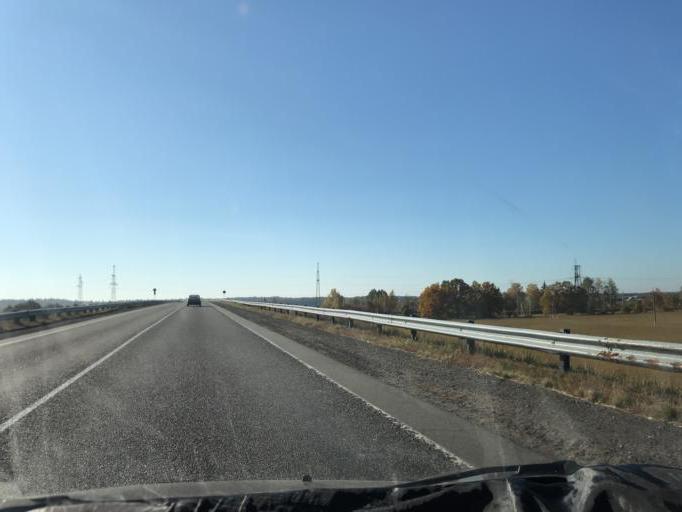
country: BY
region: Mogilev
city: Babruysk
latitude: 53.1839
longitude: 29.0486
